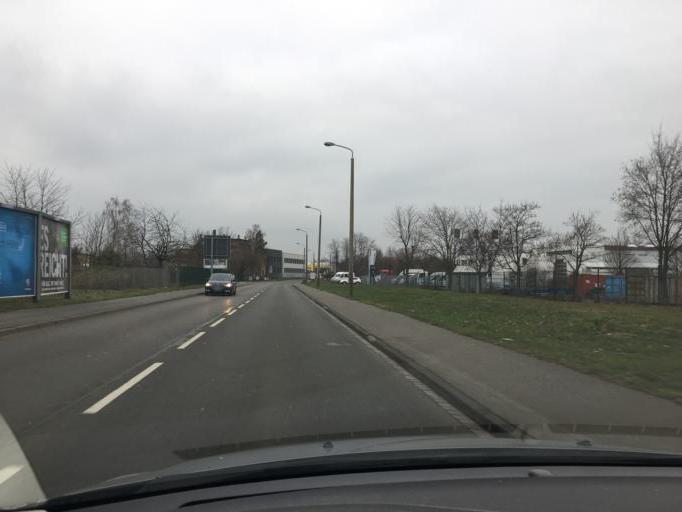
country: DE
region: Saxony
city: Taucha
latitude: 51.3414
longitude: 12.4453
